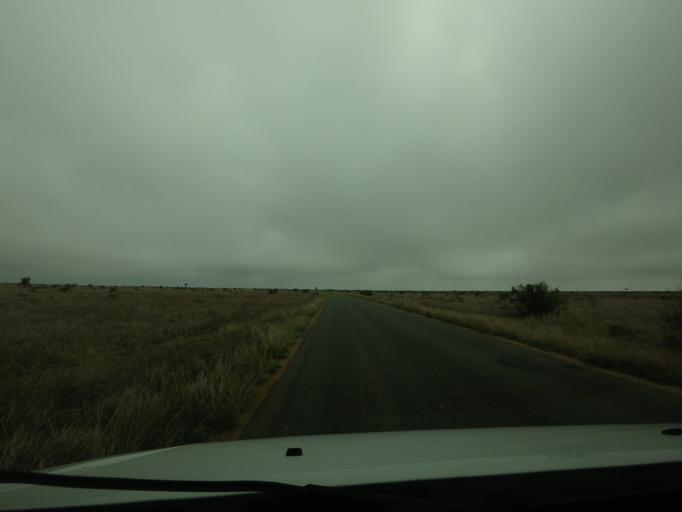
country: ZA
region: Limpopo
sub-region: Mopani District Municipality
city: Phalaborwa
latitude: -24.2276
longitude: 31.7217
